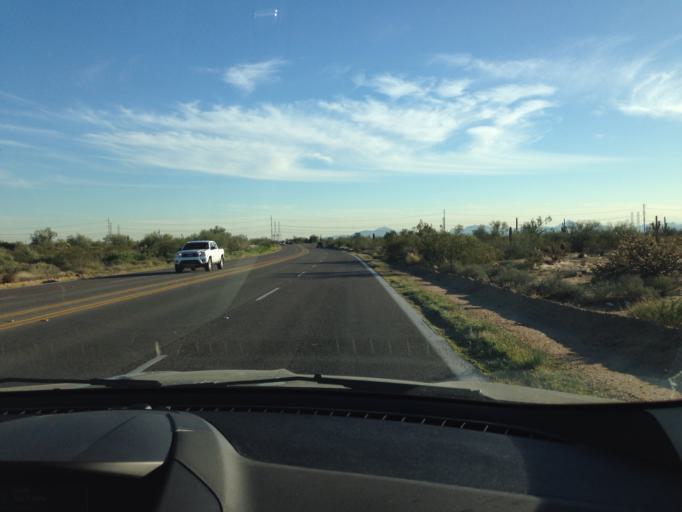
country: US
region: Arizona
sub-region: Maricopa County
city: Cave Creek
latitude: 33.7191
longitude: -111.9775
